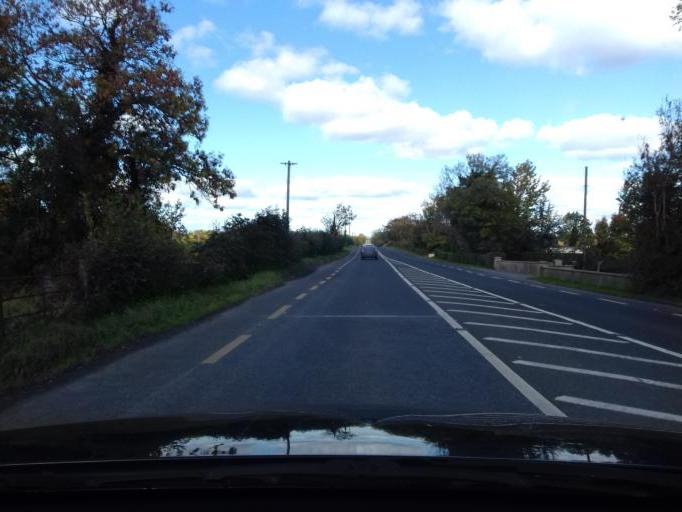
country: IE
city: Kentstown
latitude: 53.6676
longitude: -6.5310
